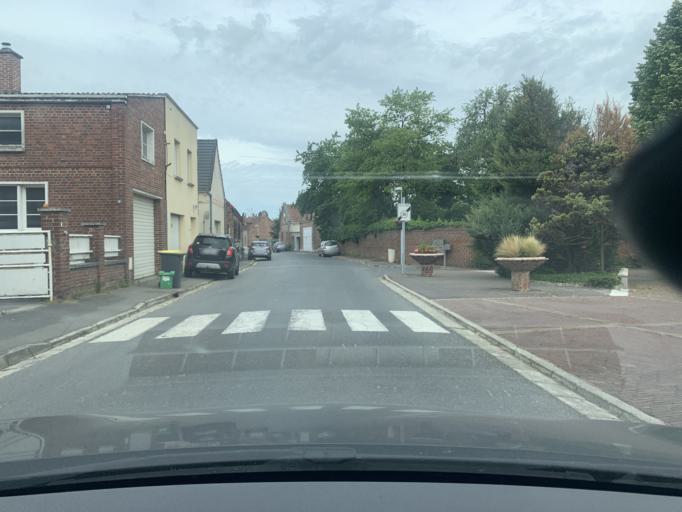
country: FR
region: Nord-Pas-de-Calais
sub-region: Departement du Nord
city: Marcoing
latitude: 50.1384
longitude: 3.1832
